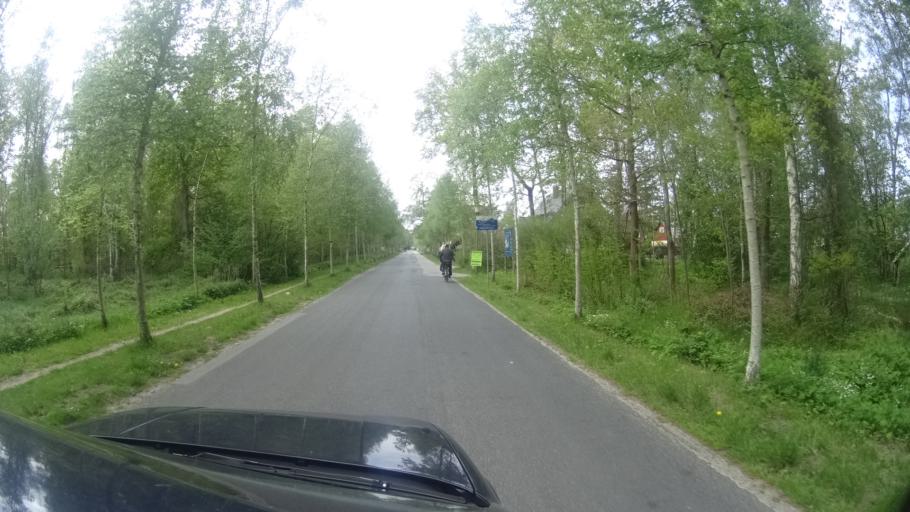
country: DE
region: Mecklenburg-Vorpommern
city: Ostseebad Dierhagen
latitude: 54.2813
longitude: 12.3199
